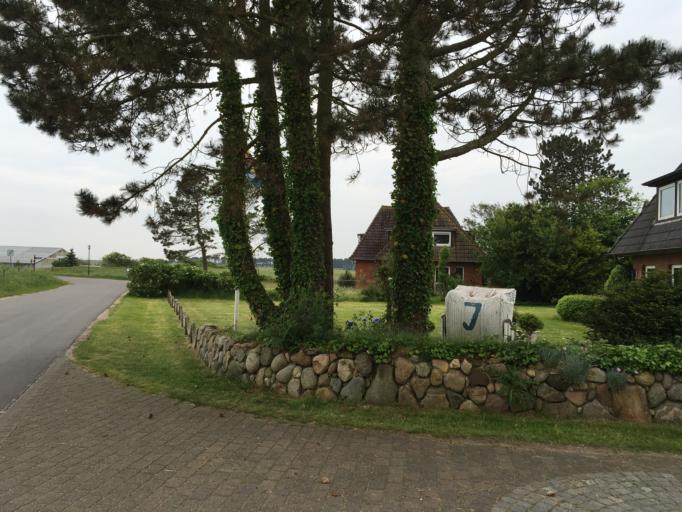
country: DE
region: Schleswig-Holstein
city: Norddorf
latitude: 54.6777
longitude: 8.3385
